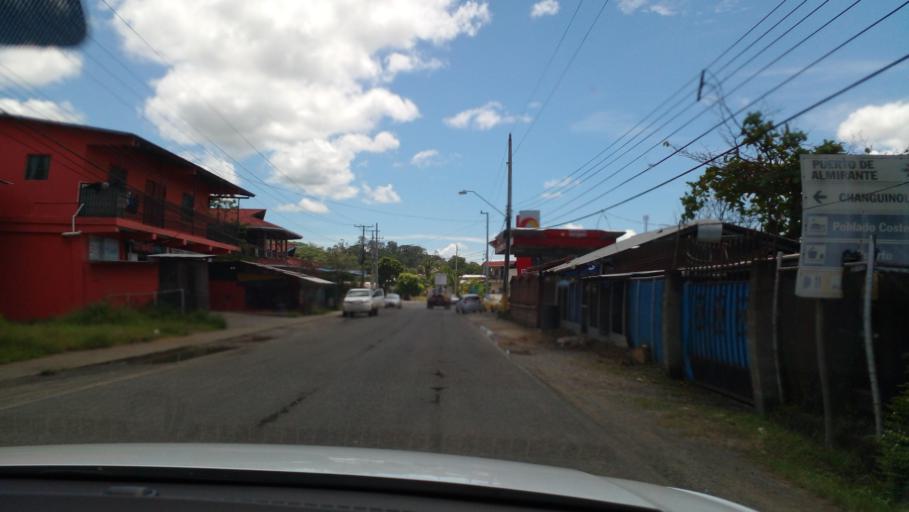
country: PA
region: Bocas del Toro
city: Almirante
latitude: 9.2961
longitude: -82.4091
